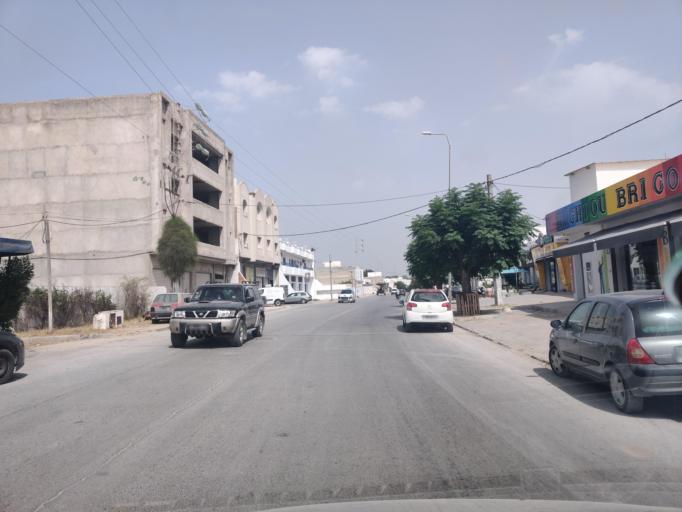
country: TN
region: Nabul
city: Al Hammamat
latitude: 36.4124
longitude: 10.5981
